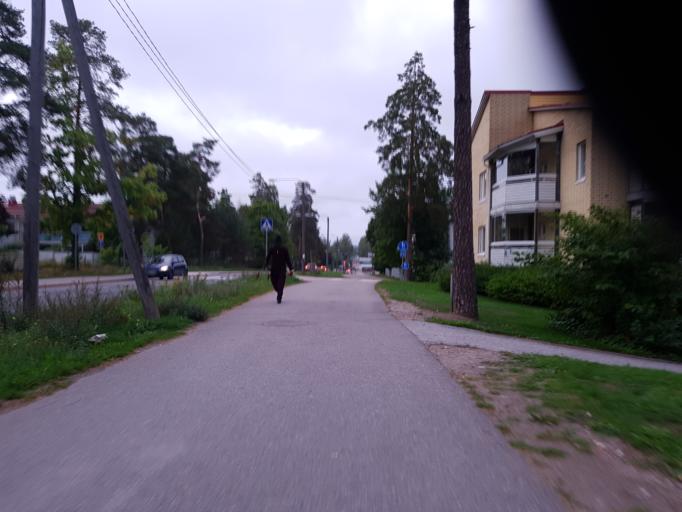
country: FI
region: Uusimaa
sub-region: Helsinki
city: Kilo
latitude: 60.2316
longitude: 24.8139
